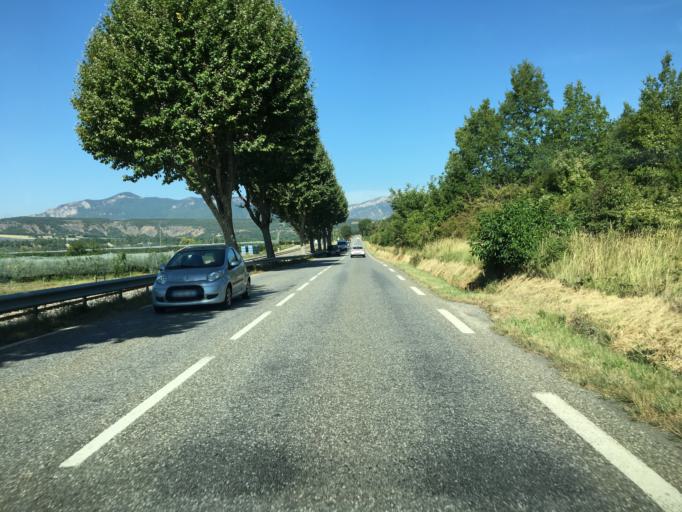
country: FR
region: Provence-Alpes-Cote d'Azur
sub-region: Departement des Hautes-Alpes
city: Laragne-Monteglin
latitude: 44.3203
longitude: 5.8062
